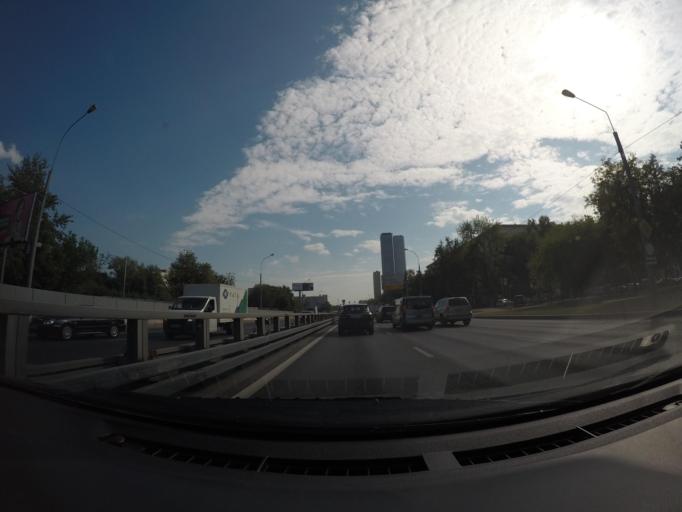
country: RU
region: Moscow
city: Novovladykino
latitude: 55.8153
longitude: 37.5767
